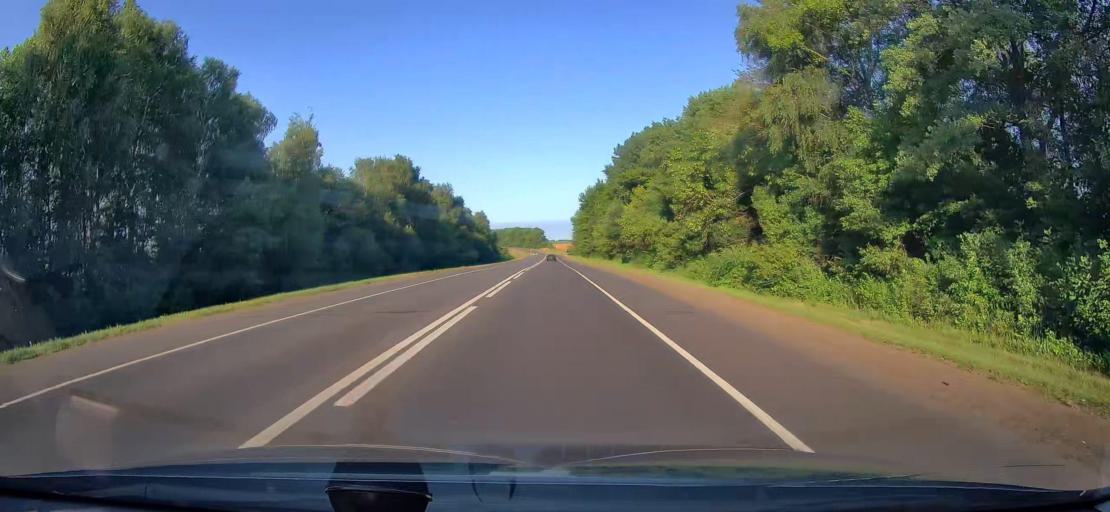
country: RU
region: Tula
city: Plavsk
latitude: 53.6804
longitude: 37.2558
